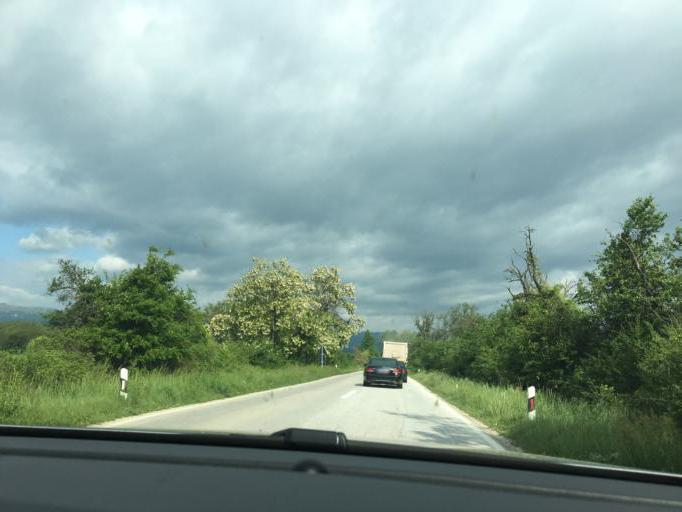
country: MK
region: Resen
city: Resen
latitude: 41.0658
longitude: 21.0471
